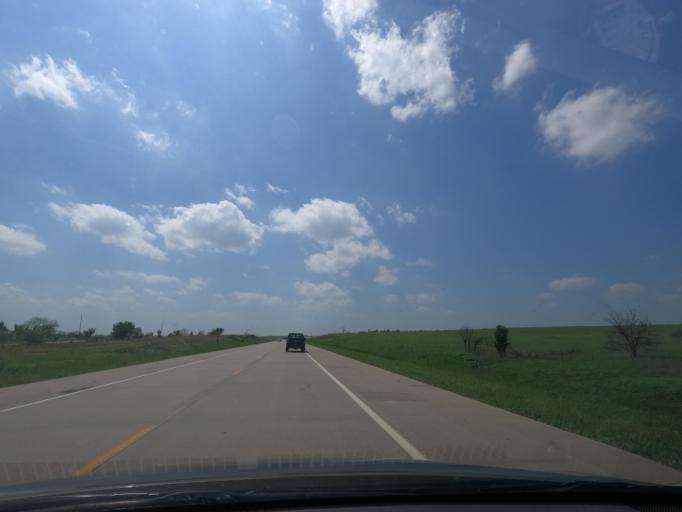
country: US
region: Kansas
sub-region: Elk County
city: Howard
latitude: 37.6280
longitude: -96.1311
